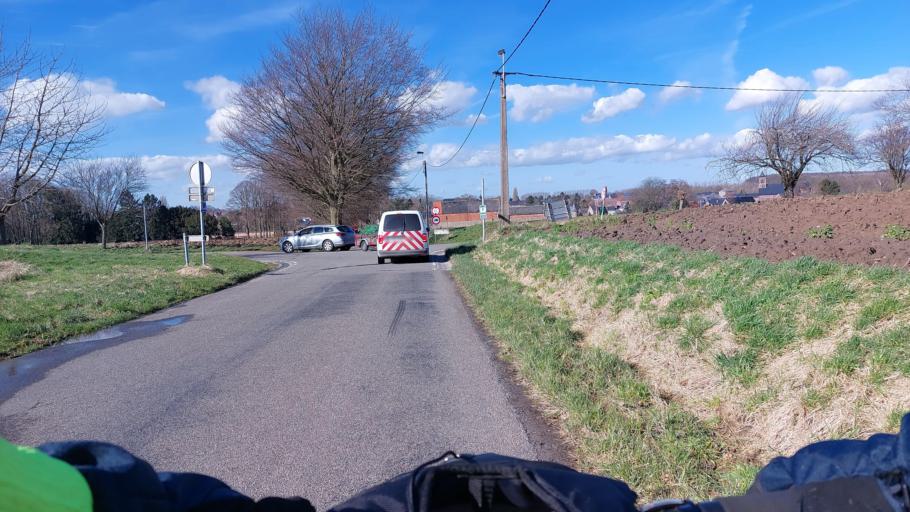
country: BE
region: Wallonia
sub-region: Province du Hainaut
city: Ecaussinnes-d'Enghien
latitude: 50.5660
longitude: 4.1812
